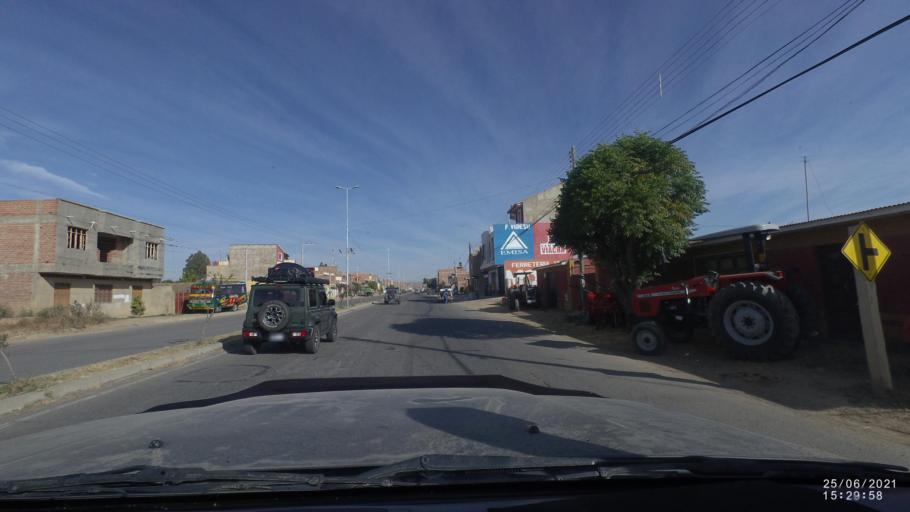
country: BO
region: Cochabamba
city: Cliza
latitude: -17.5790
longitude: -65.9340
